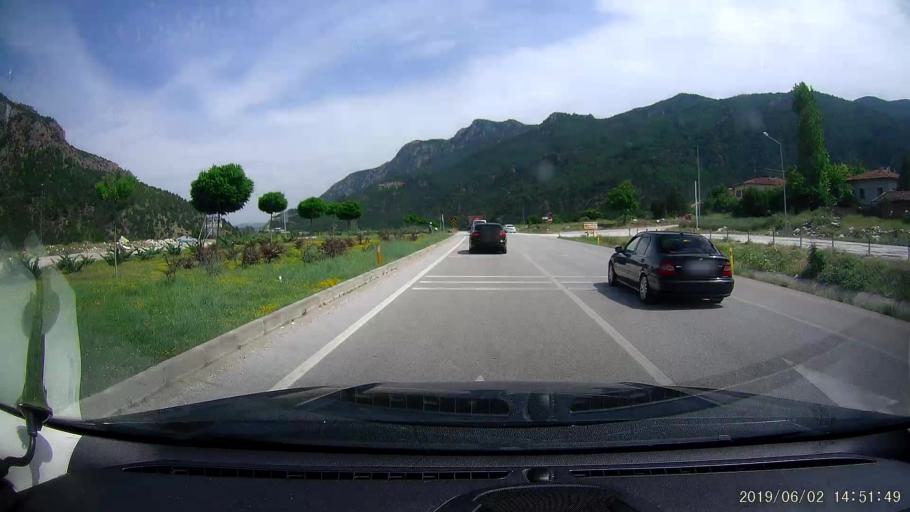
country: TR
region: Corum
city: Hacihamza
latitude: 41.0544
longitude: 34.5448
